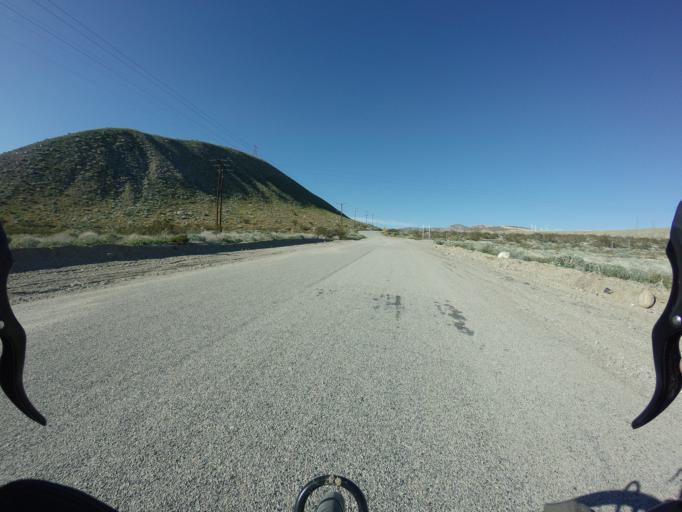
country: US
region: California
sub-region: Riverside County
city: Garnet
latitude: 33.9252
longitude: -116.6418
